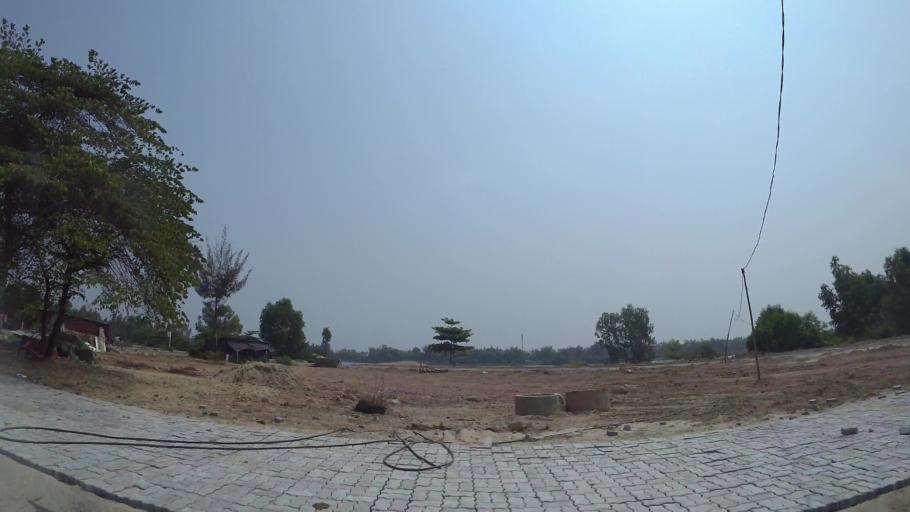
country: VN
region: Da Nang
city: Cam Le
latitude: 15.9791
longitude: 108.2197
